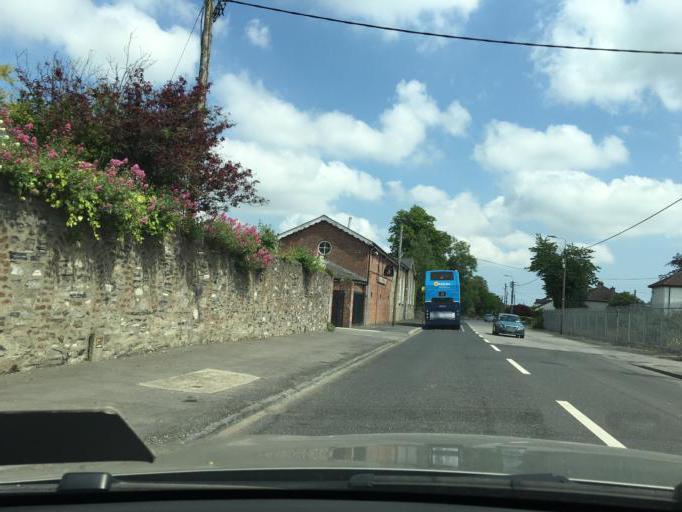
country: IE
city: Palmerstown
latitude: 53.3580
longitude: -6.3799
